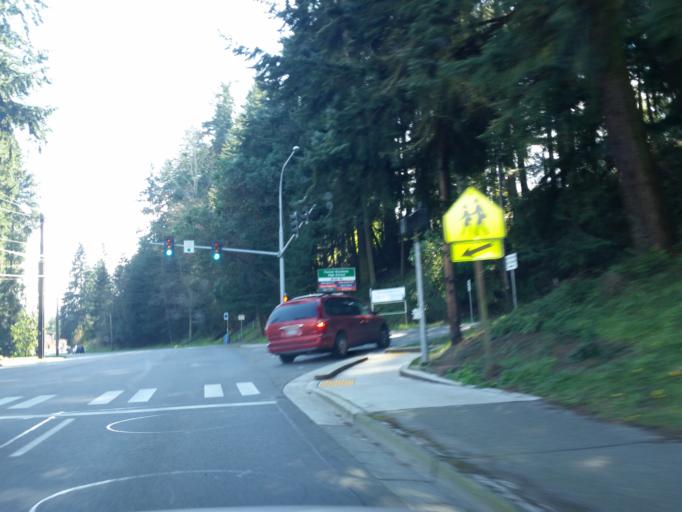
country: US
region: Washington
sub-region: Snohomish County
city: Esperance
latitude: 47.7884
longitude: -122.3669
